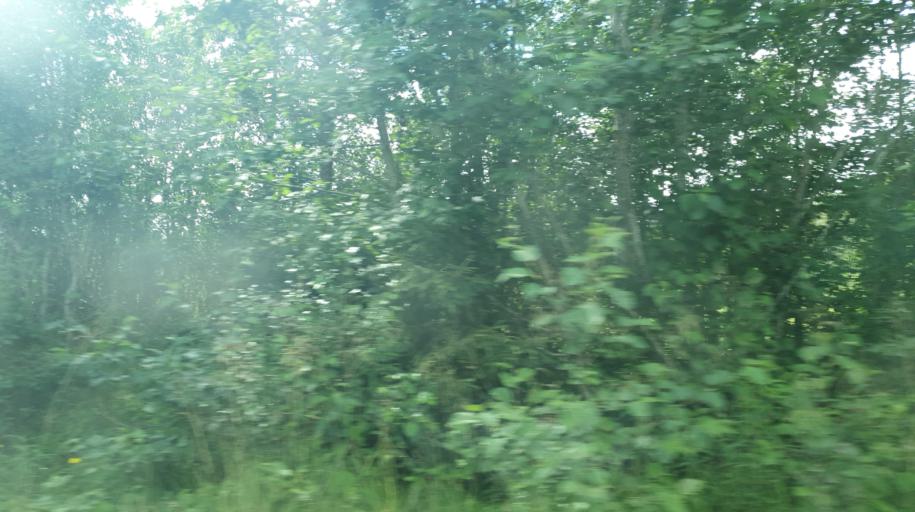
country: NO
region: Nord-Trondelag
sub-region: Levanger
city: Skogn
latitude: 63.5828
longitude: 11.2456
